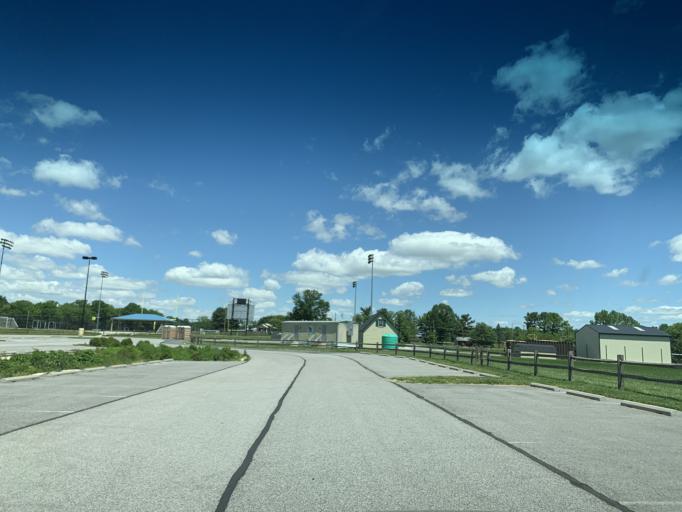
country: US
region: Pennsylvania
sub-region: Chester County
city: Oxford
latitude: 39.6990
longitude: -75.9724
